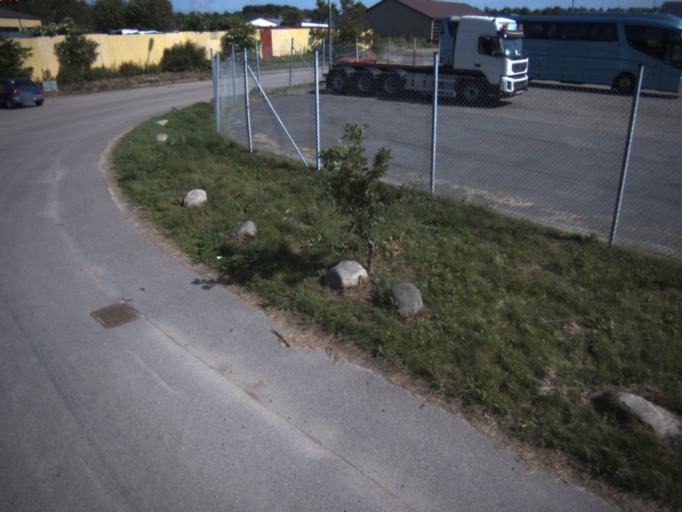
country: SE
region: Skane
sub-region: Helsingborg
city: Odakra
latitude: 56.0658
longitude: 12.7608
